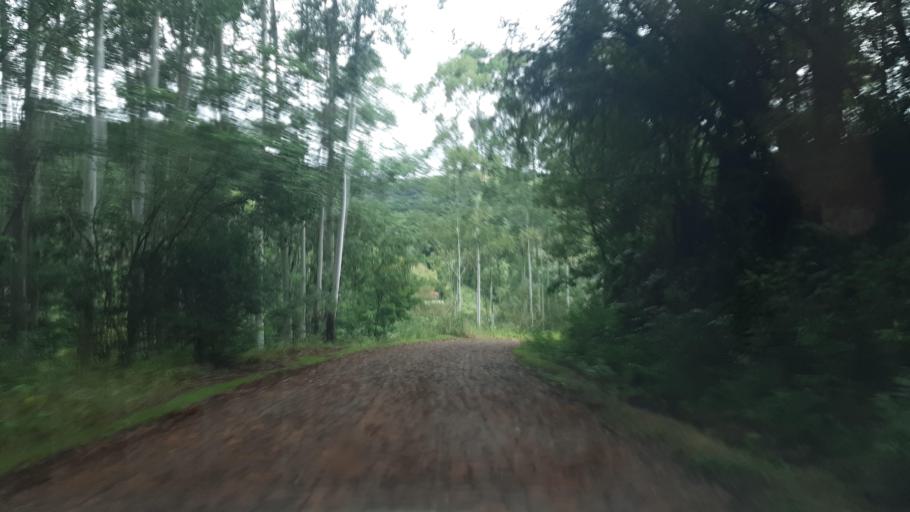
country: BR
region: Parana
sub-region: Ampere
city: Ampere
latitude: -26.0408
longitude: -53.5136
